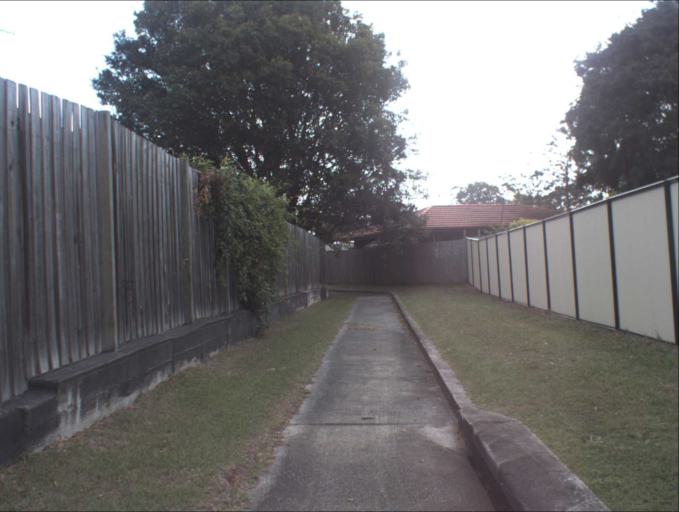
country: AU
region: Queensland
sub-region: Logan
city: Waterford West
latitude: -27.6788
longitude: 153.1314
